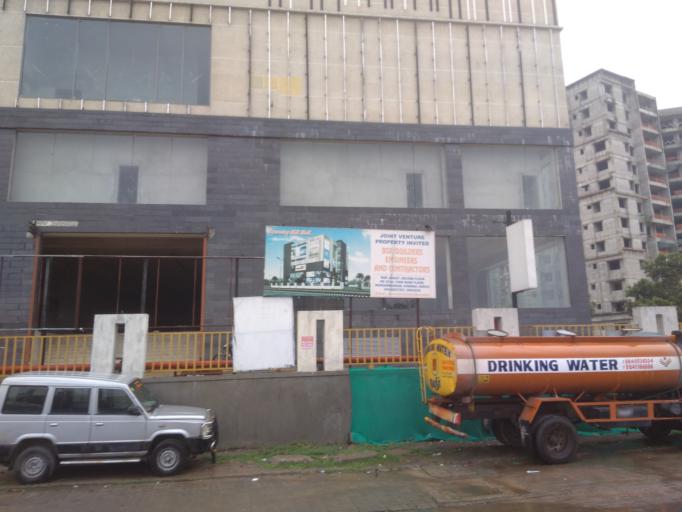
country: IN
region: Tamil Nadu
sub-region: Kancheepuram
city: Perungudi
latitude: 12.9496
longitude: 80.2408
